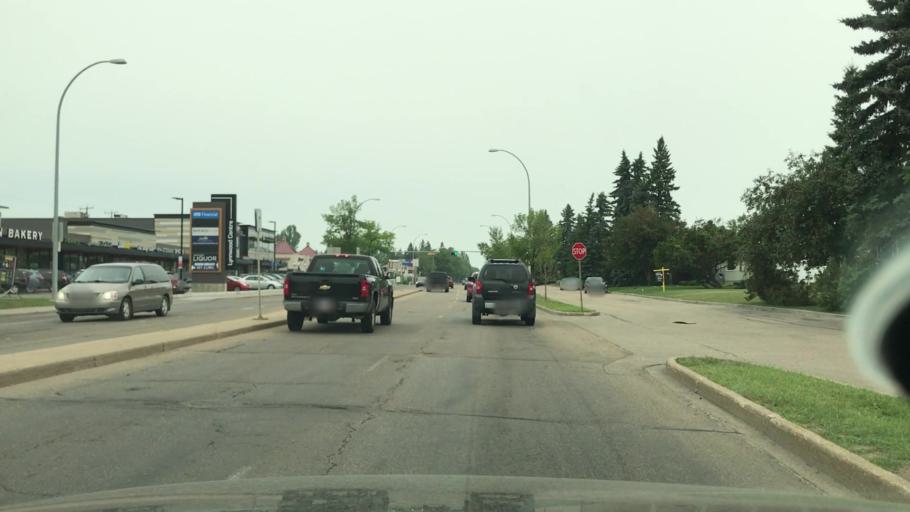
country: CA
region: Alberta
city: Edmonton
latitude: 53.5197
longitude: -113.5778
